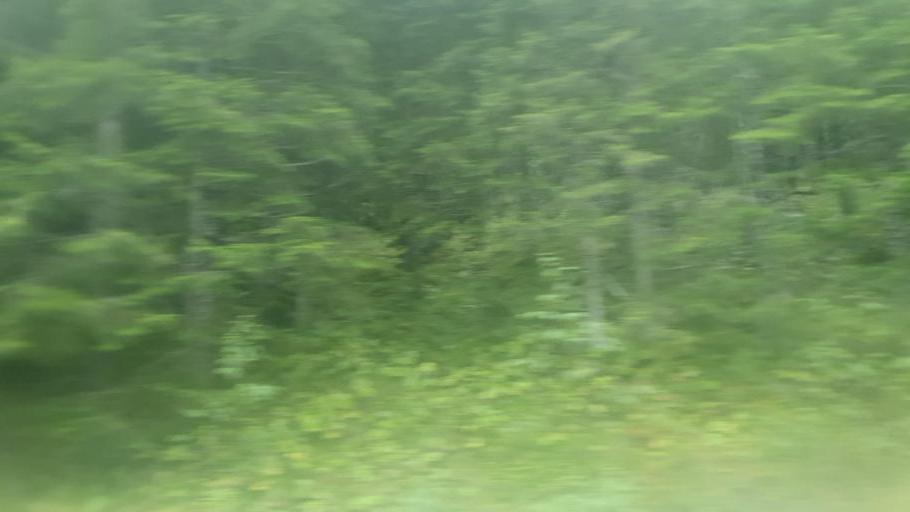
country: NO
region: Nord-Trondelag
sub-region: Levanger
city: Skogn
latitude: 63.6175
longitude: 11.2189
